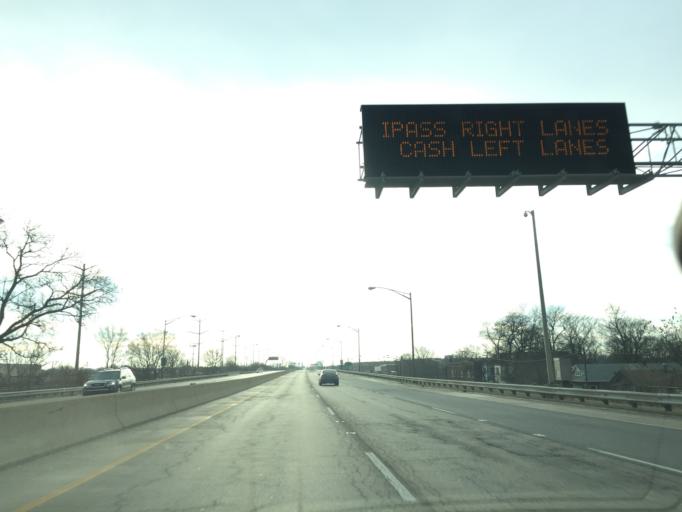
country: US
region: Indiana
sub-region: Lake County
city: Whiting
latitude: 41.7440
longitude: -87.5778
